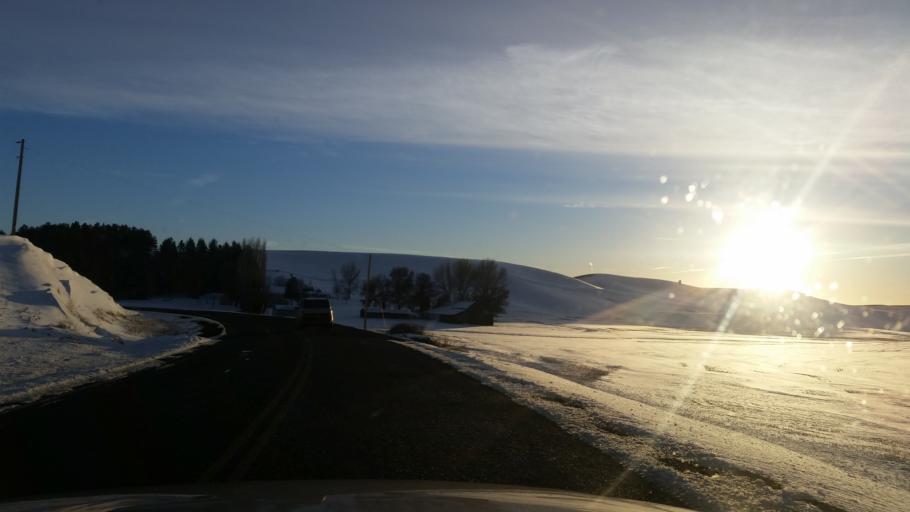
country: US
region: Washington
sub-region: Whitman County
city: Colfax
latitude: 47.1472
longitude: -117.5566
